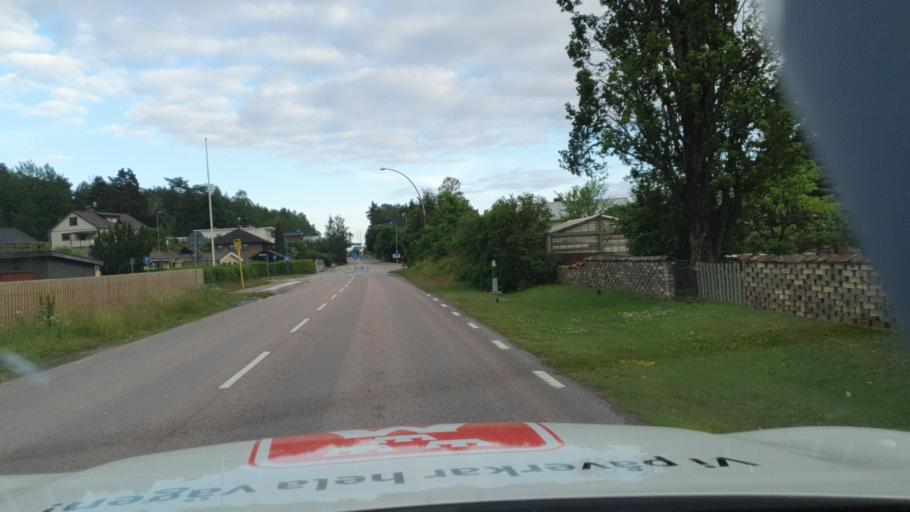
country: SE
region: Vaermland
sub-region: Karlstads Kommun
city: Karlstad
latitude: 59.4003
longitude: 13.5141
